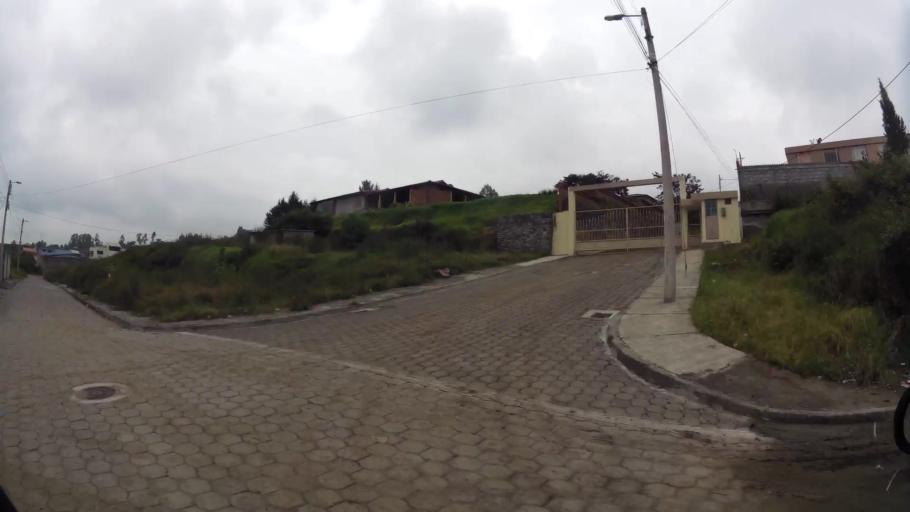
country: EC
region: Pichincha
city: Quito
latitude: -0.2679
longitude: -78.4771
